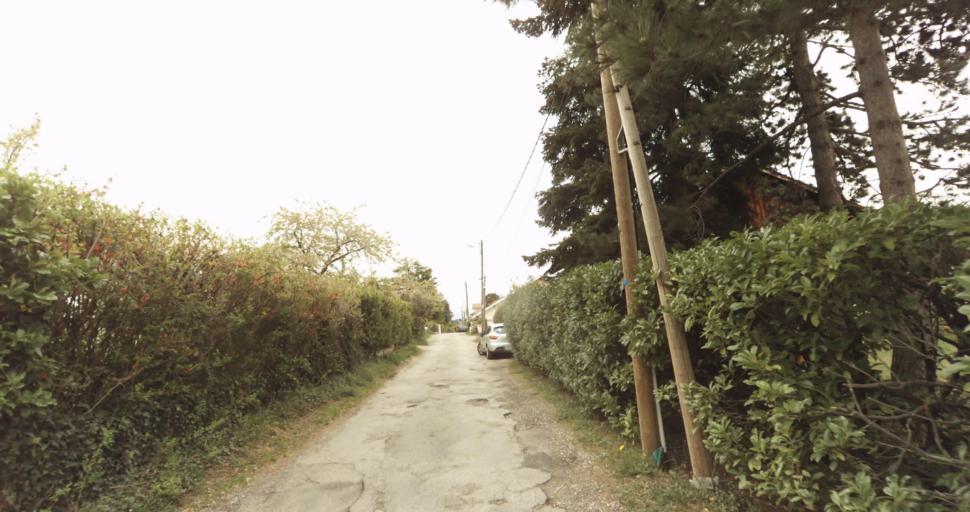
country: FR
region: Rhone-Alpes
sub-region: Departement de l'Isere
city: Biviers
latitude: 45.2291
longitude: 5.7999
